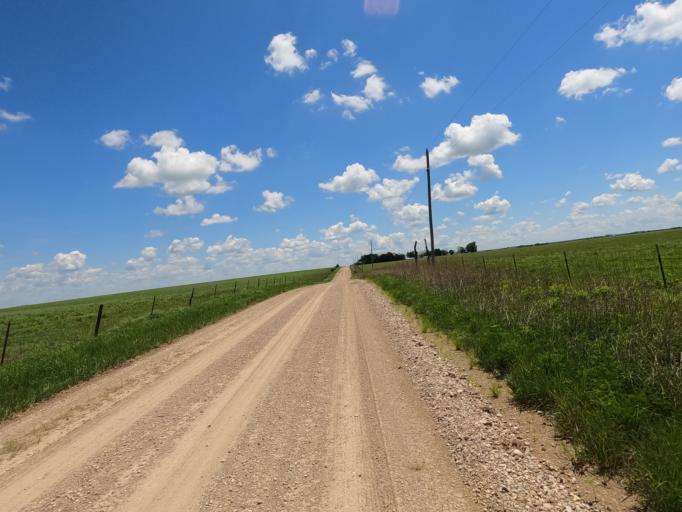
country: US
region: Kansas
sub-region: Chase County
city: Cottonwood Falls
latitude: 38.2168
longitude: -96.7383
